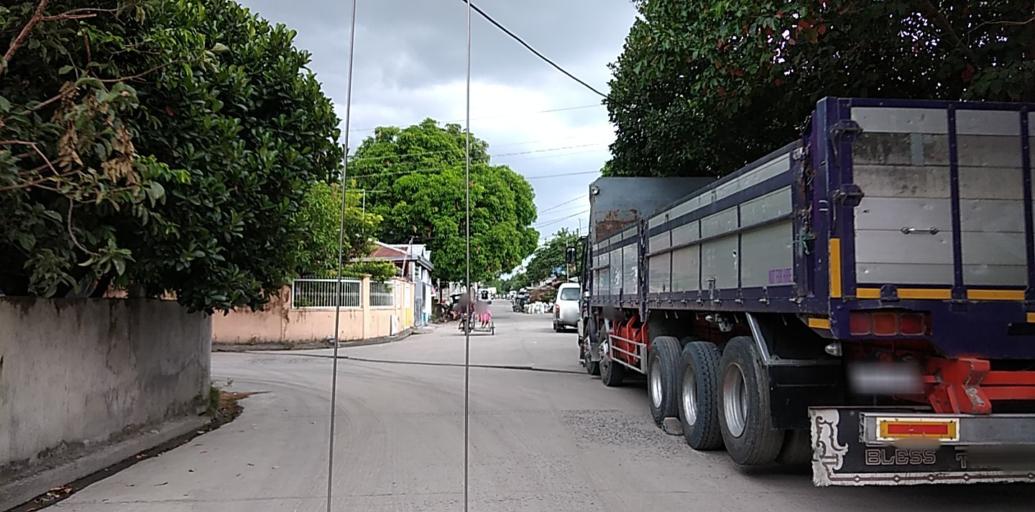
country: PH
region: Central Luzon
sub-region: Province of Pampanga
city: Pio
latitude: 15.0408
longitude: 120.5295
